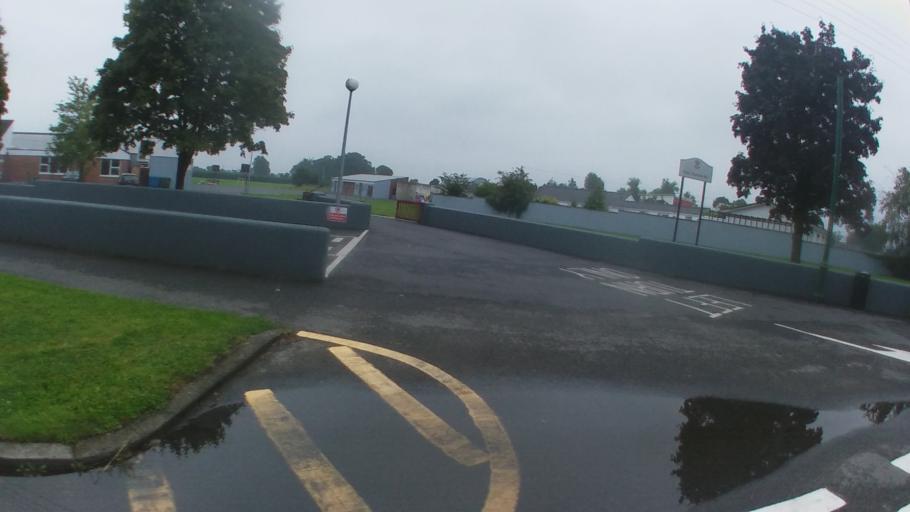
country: IE
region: Leinster
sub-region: Kilkenny
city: Callan
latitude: 52.5498
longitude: -7.3862
